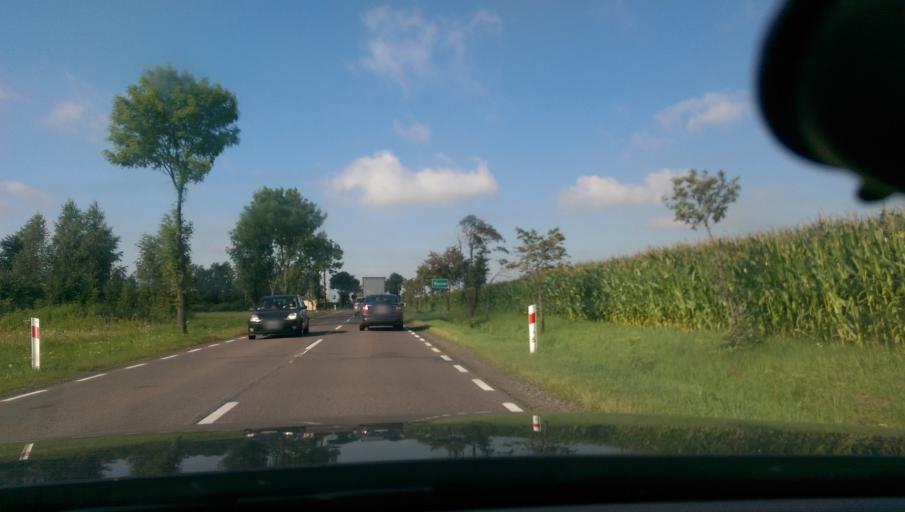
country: PL
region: Masovian Voivodeship
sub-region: Powiat plonski
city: Sochocin
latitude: 52.6638
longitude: 20.4459
